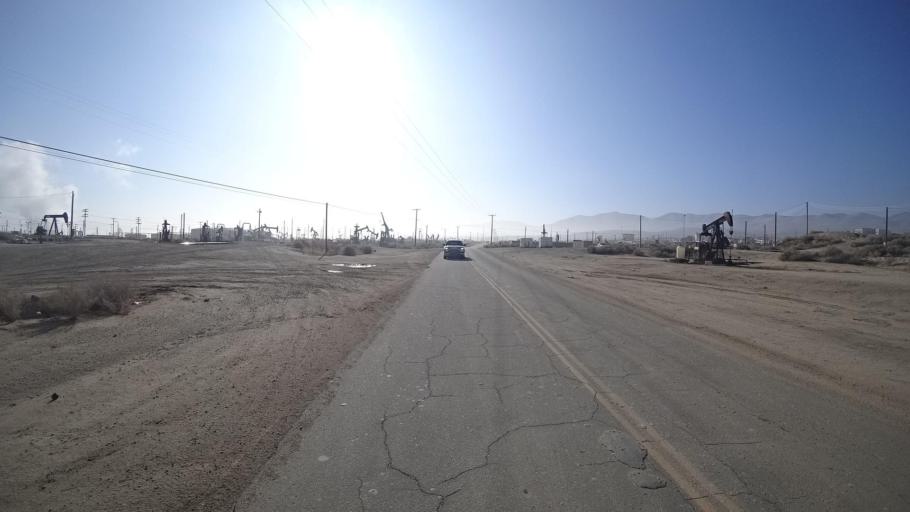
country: US
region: California
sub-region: Kern County
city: Taft Heights
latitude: 35.2177
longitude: -119.5984
